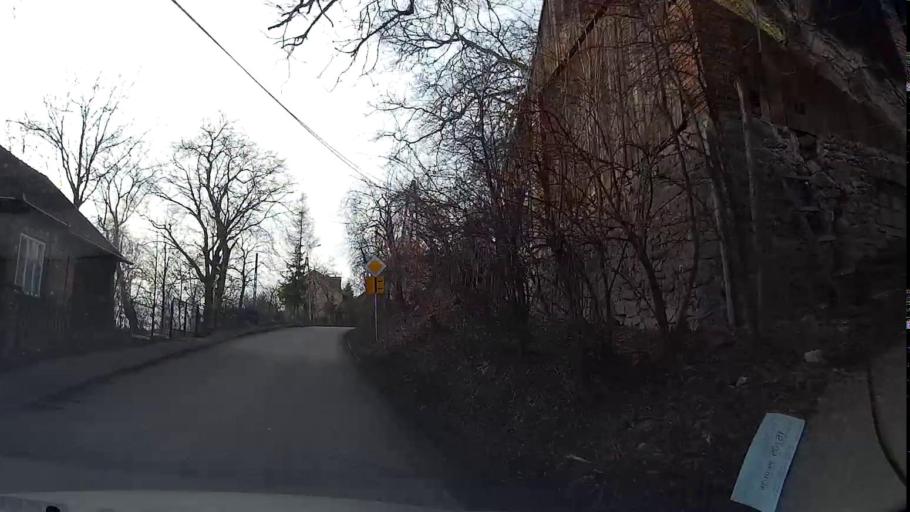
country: PL
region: Lesser Poland Voivodeship
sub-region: Powiat krakowski
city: Czulow
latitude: 50.0613
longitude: 19.6931
